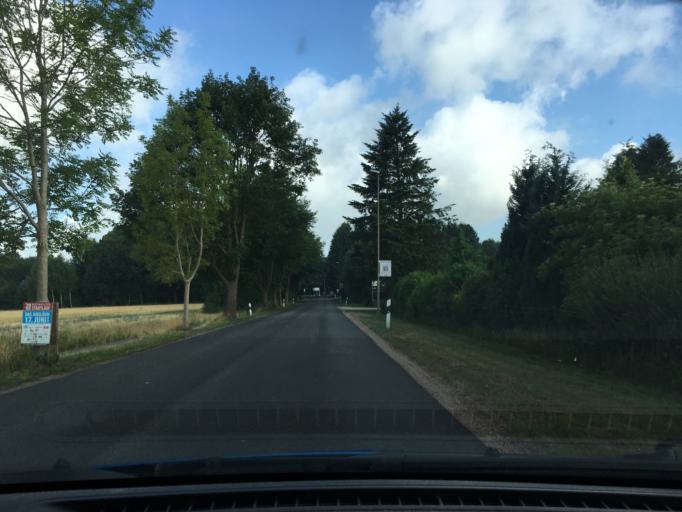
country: DE
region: Lower Saxony
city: Buchholz in der Nordheide
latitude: 53.3288
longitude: 9.8345
